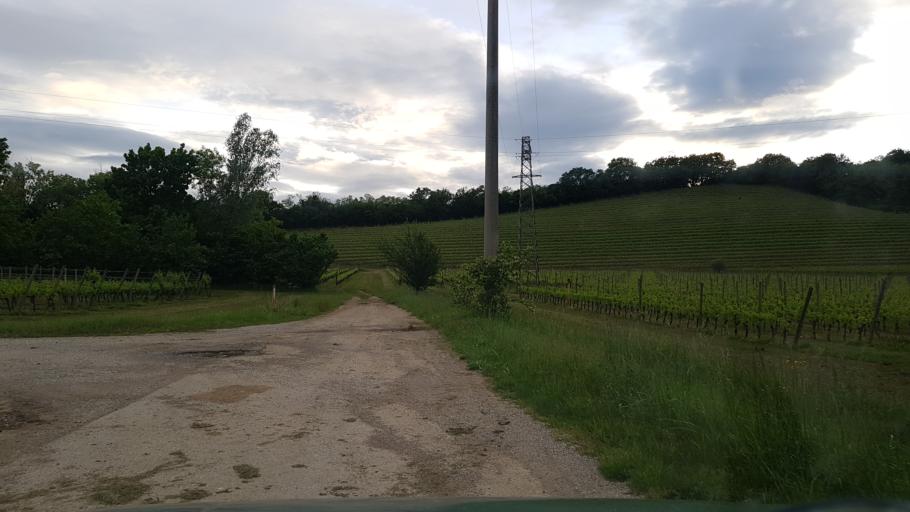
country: IT
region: Friuli Venezia Giulia
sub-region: Provincia di Gorizia
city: Farra d'Isonzo
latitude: 45.9100
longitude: 13.5292
